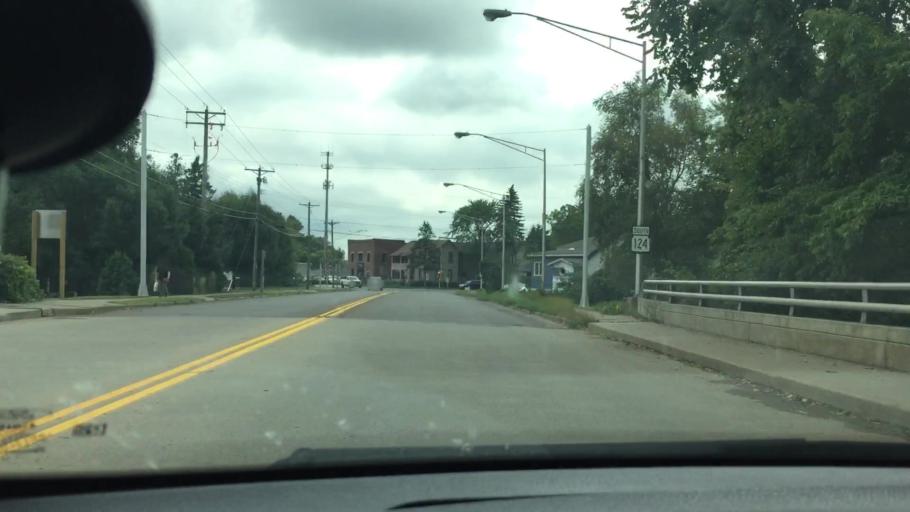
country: US
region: Wisconsin
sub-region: Chippewa County
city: Chippewa Falls
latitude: 44.9438
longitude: -91.3963
